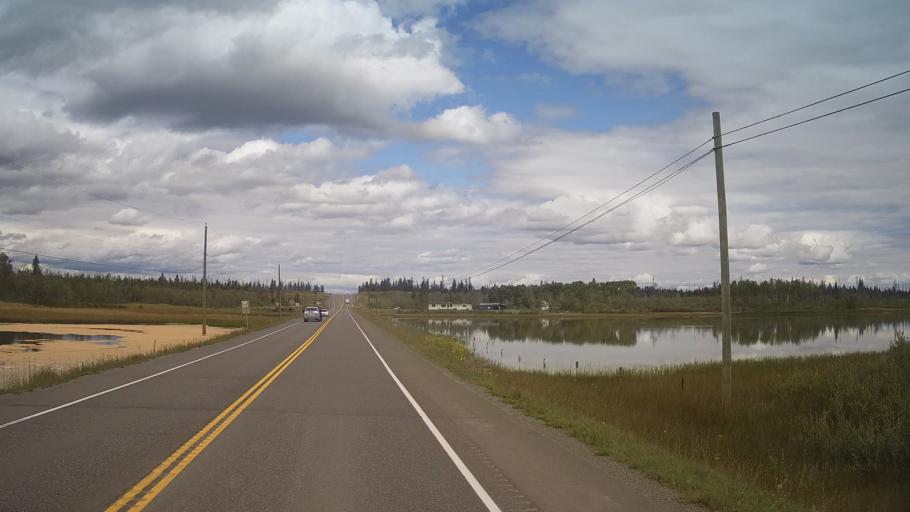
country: CA
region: British Columbia
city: Cache Creek
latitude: 51.3185
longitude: -121.3894
